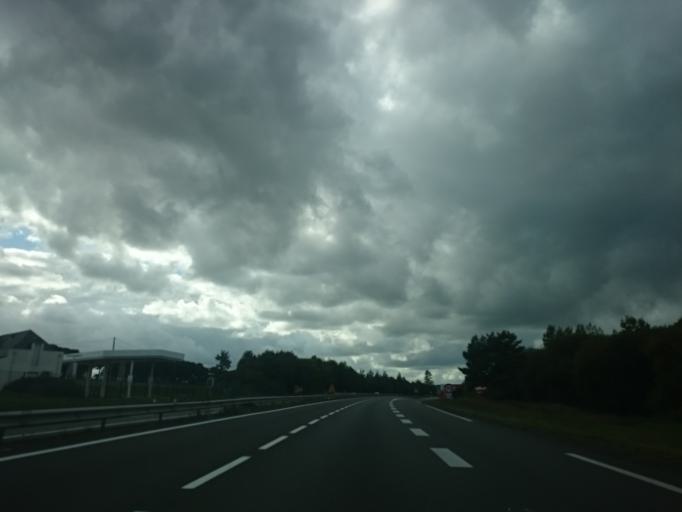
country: FR
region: Brittany
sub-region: Departement des Cotes-d'Armor
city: Caulnes
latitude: 48.2722
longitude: -2.1720
